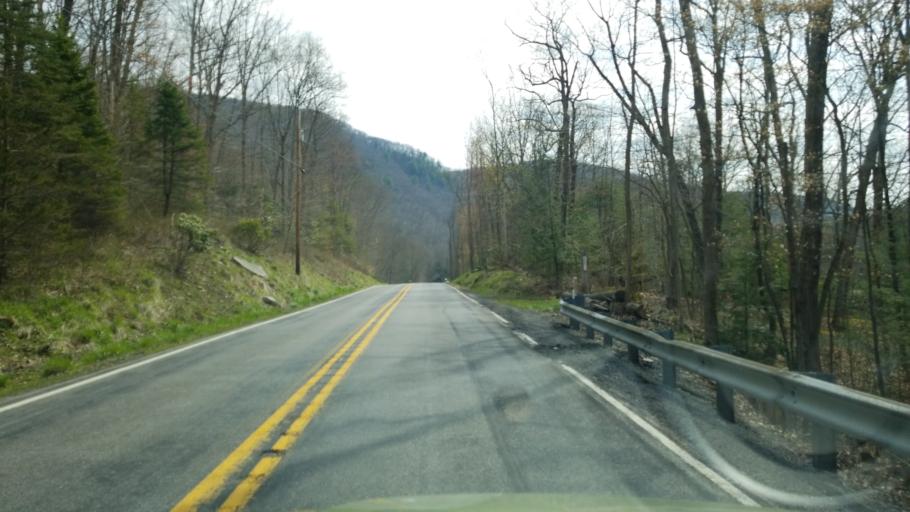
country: US
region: Pennsylvania
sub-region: Clinton County
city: Renovo
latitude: 41.3004
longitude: -77.9933
